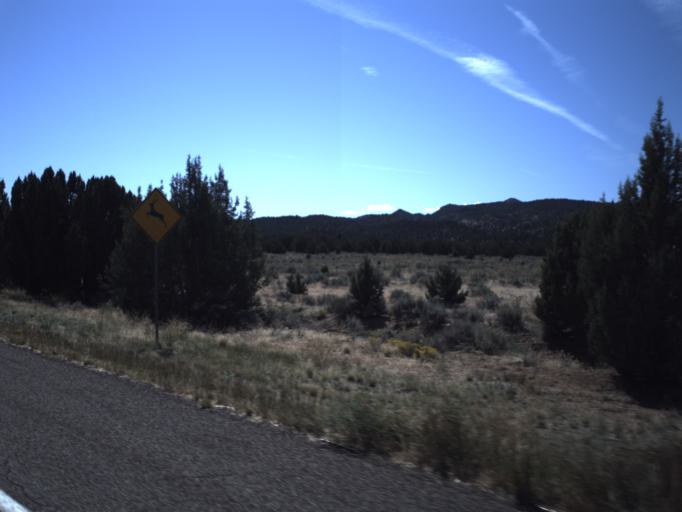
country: US
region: Utah
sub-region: Washington County
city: Ivins
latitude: 37.2970
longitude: -113.6646
